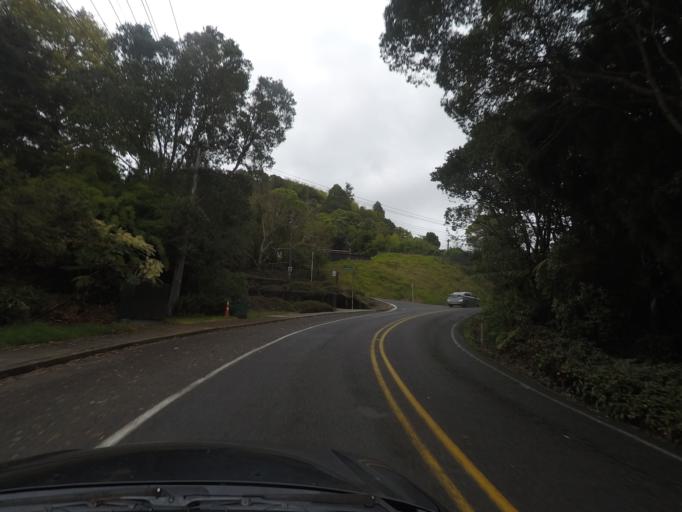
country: NZ
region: Auckland
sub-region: Auckland
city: Titirangi
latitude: -36.9325
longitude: 174.5884
